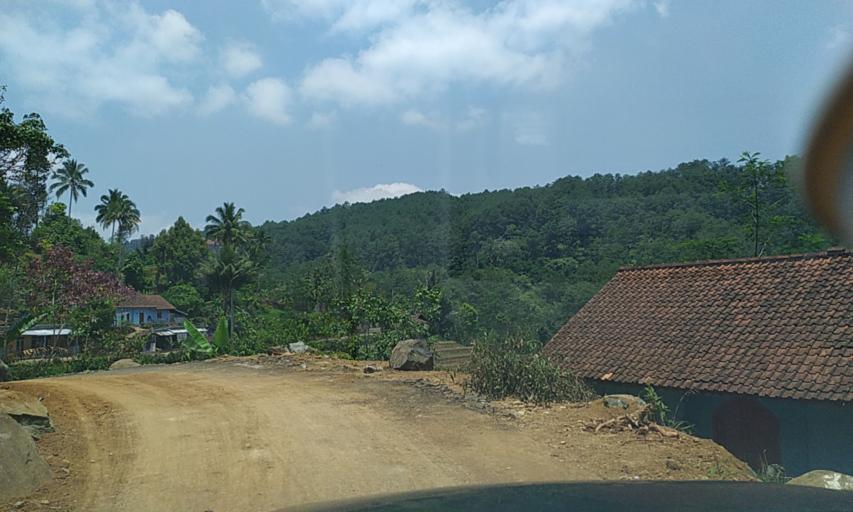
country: ID
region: Central Java
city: Kaduluhur
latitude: -7.1891
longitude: 108.6486
